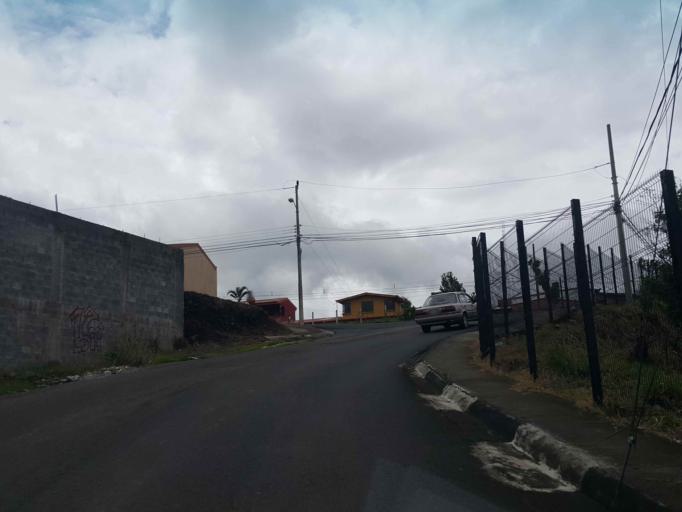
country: CR
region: Heredia
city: San Josecito
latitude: 10.0215
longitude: -84.1110
